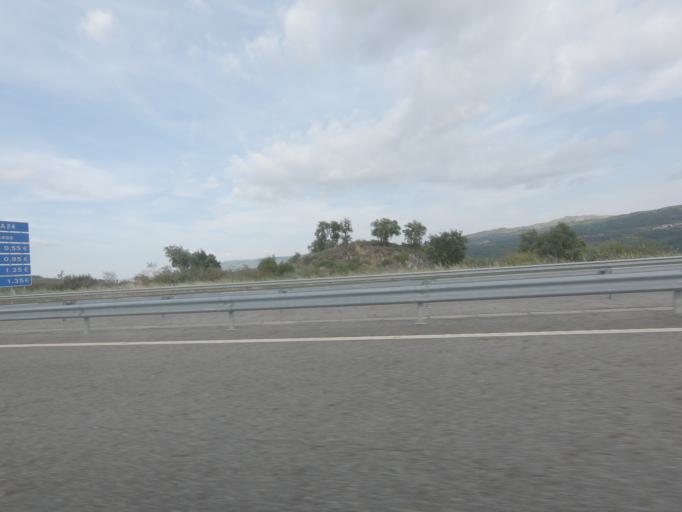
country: PT
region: Vila Real
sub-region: Chaves
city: Chaves
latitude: 41.7024
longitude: -7.5494
